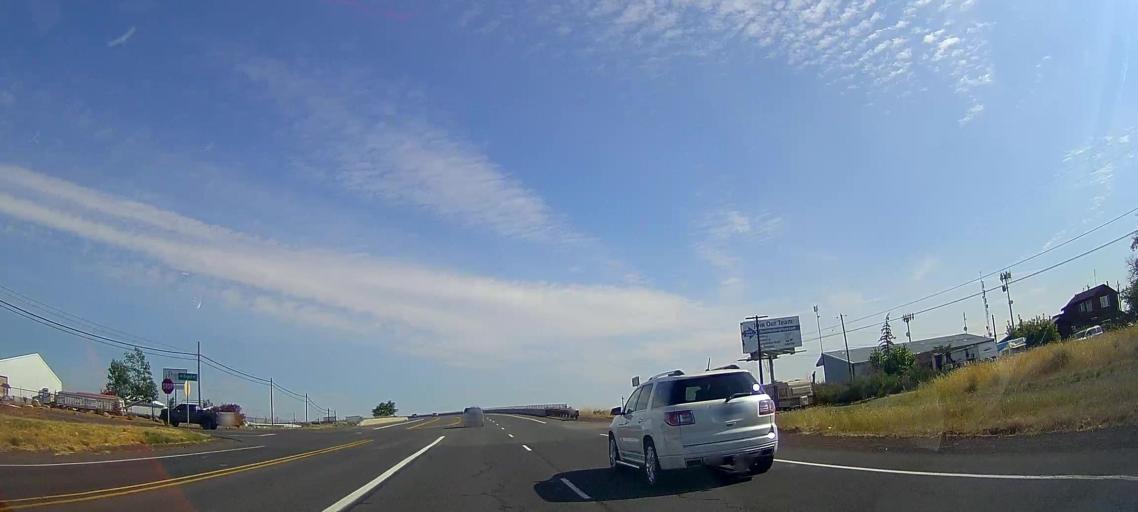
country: US
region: Oregon
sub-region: Jefferson County
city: Madras
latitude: 44.6518
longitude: -121.1286
